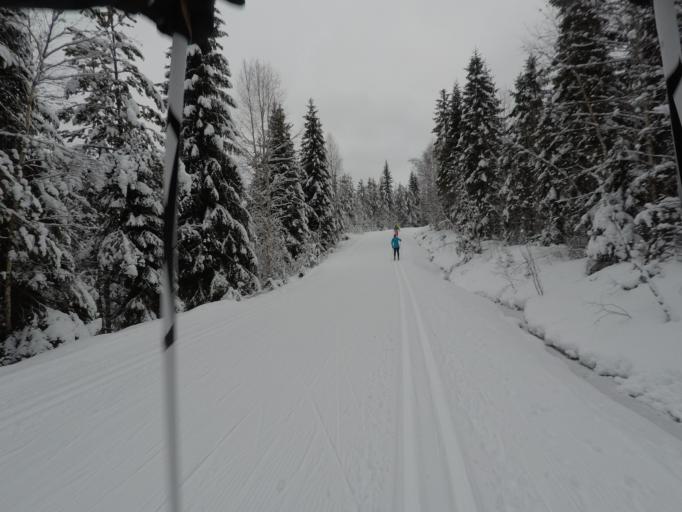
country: SE
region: Dalarna
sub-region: Ludvika Kommun
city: Abborrberget
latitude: 60.1370
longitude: 14.4839
